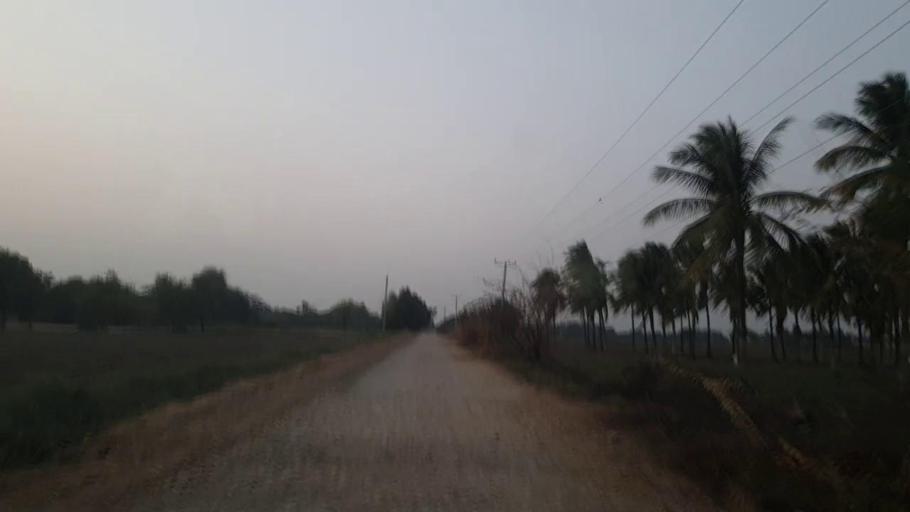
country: PK
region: Sindh
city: Mirpur Sakro
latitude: 24.5911
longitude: 67.7801
